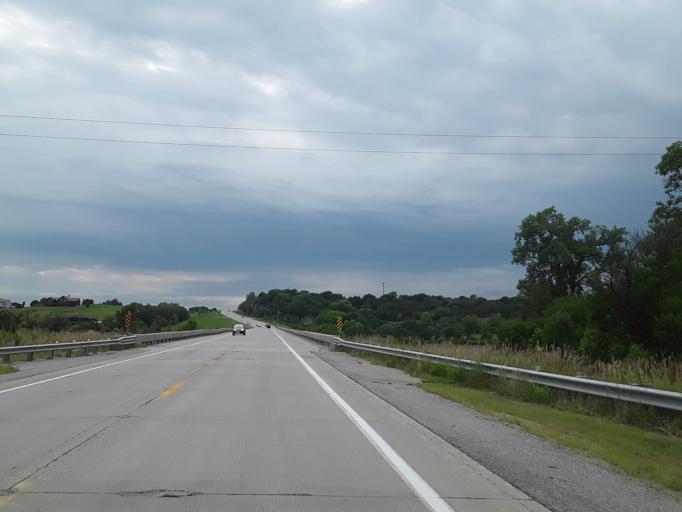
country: US
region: Nebraska
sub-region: Saunders County
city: Yutan
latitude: 41.2344
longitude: -96.3622
